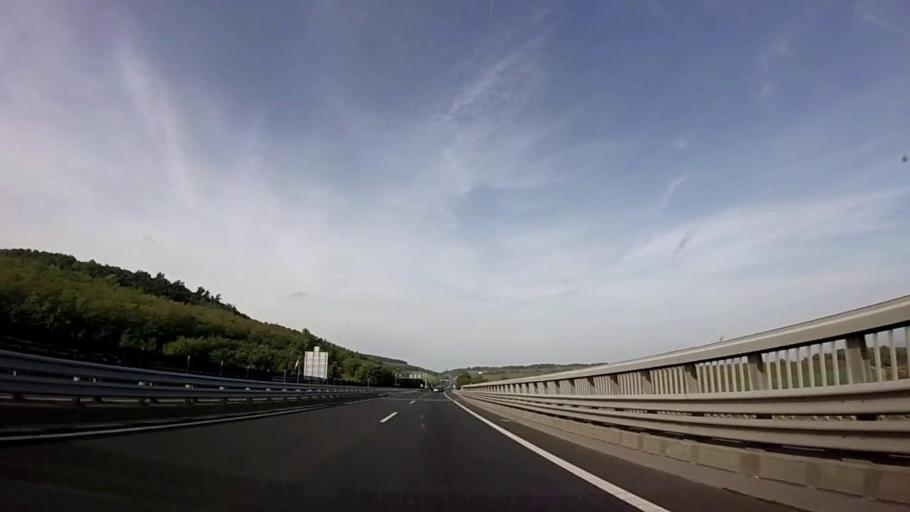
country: HU
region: Somogy
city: Balatonfoldvar
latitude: 46.8193
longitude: 17.8898
